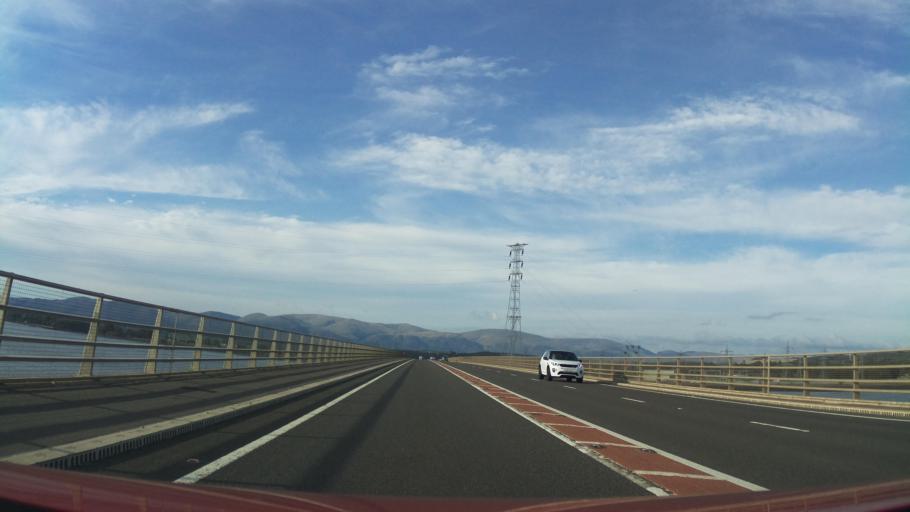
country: GB
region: Scotland
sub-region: Fife
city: Kincardine
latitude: 56.0663
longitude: -3.7315
